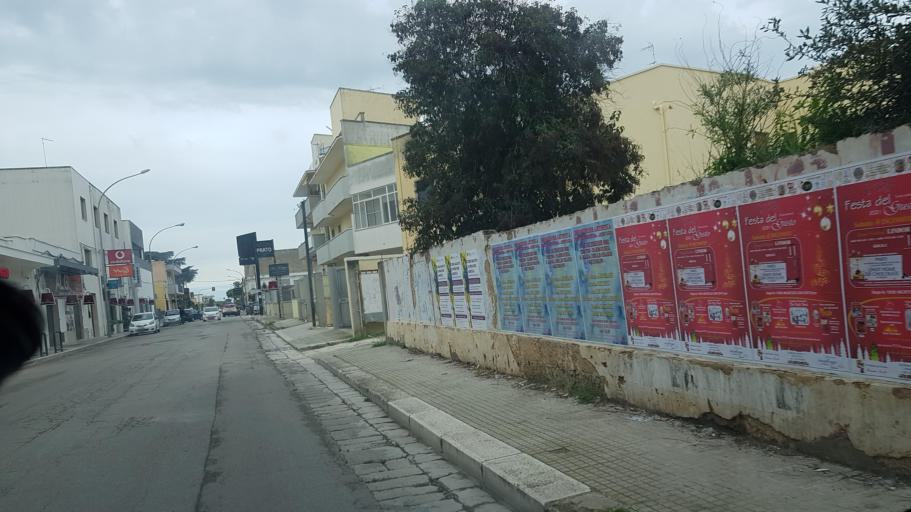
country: IT
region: Apulia
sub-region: Provincia di Lecce
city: Squinzano
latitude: 40.4386
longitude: 18.0379
